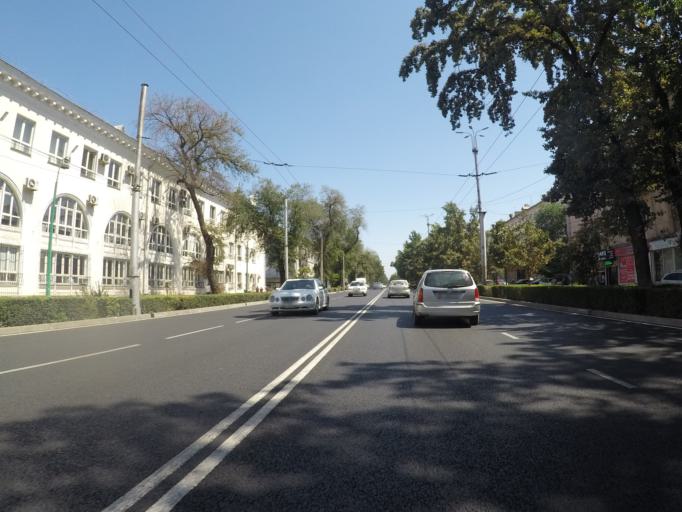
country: KG
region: Chuy
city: Bishkek
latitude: 42.8769
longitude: 74.5818
